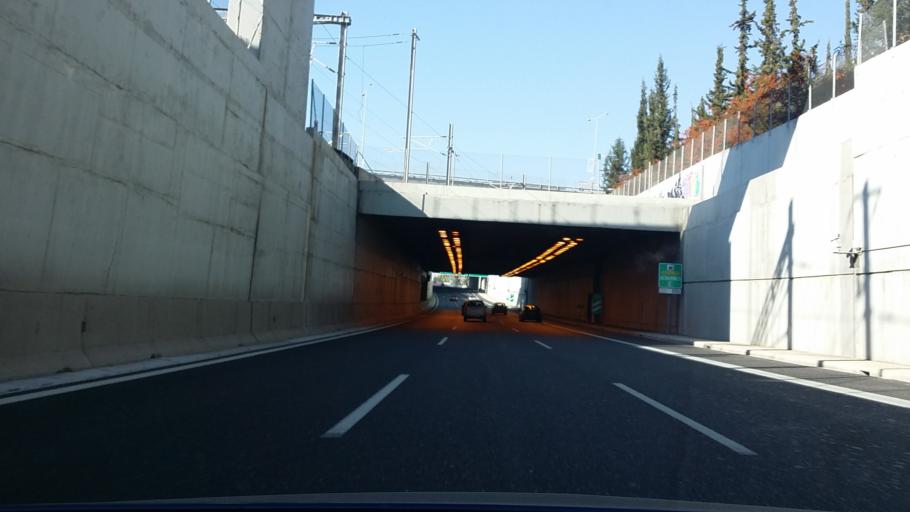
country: GR
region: Attica
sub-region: Nomarchia Anatolikis Attikis
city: Acharnes
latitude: 38.0651
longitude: 23.7403
